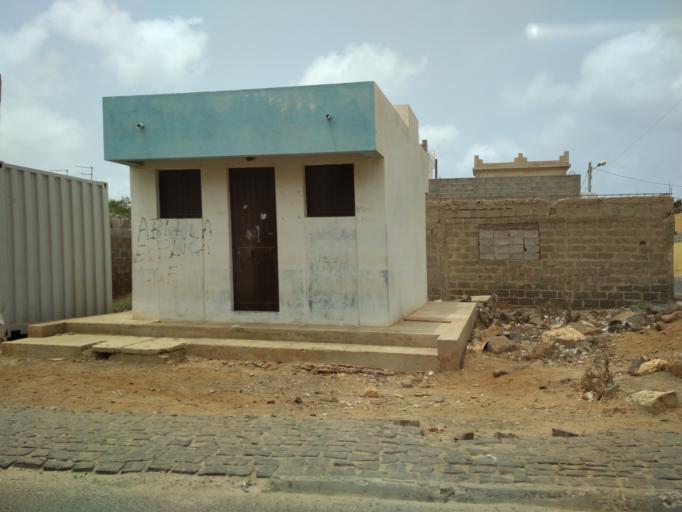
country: CV
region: Sal
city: Espargos
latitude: 16.7587
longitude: -22.9796
